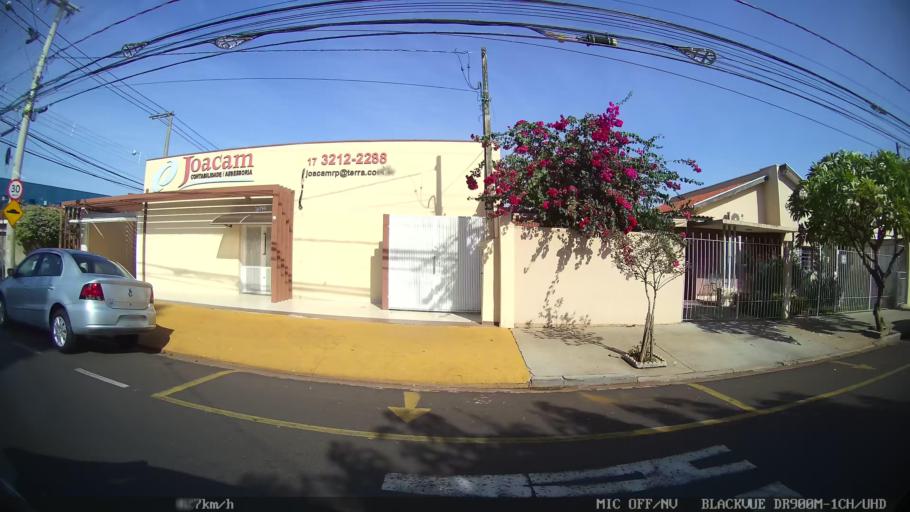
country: BR
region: Sao Paulo
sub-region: Sao Jose Do Rio Preto
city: Sao Jose do Rio Preto
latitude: -20.8079
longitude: -49.3921
